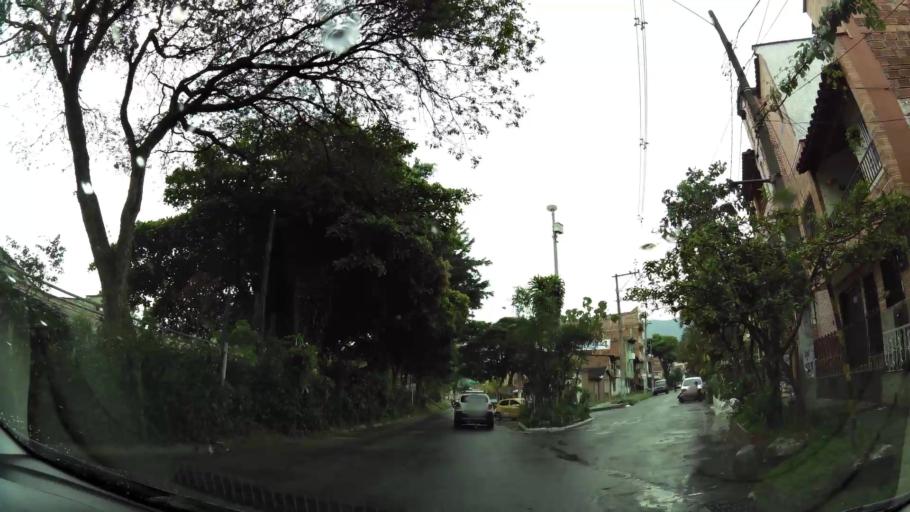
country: CO
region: Antioquia
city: Itagui
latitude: 6.1828
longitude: -75.5942
